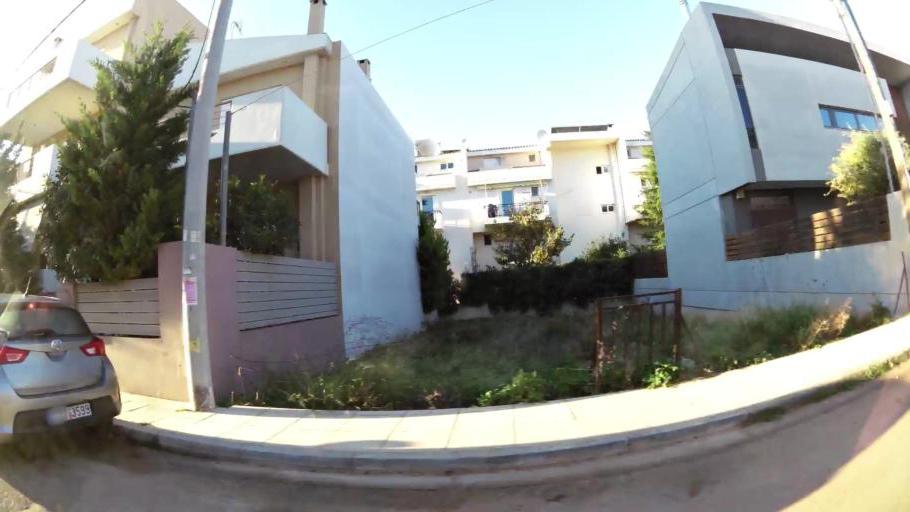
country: GR
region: Attica
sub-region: Nomarchia Anatolikis Attikis
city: Gerakas
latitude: 38.0285
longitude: 23.8495
